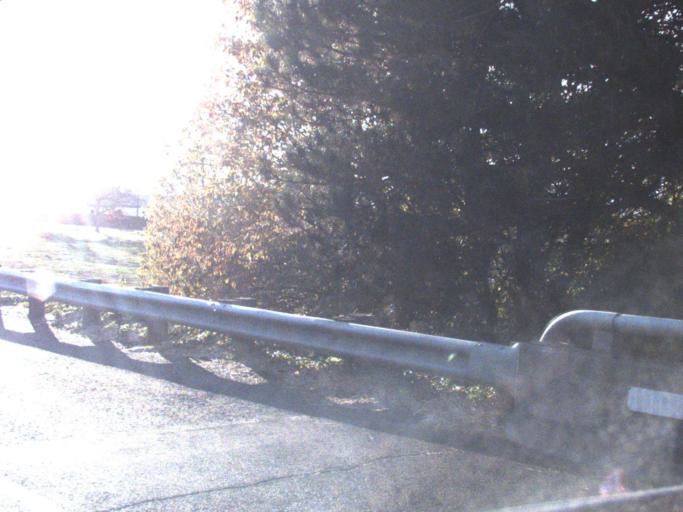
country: US
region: Washington
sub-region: Walla Walla County
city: Walla Walla
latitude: 46.0765
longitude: -118.3383
